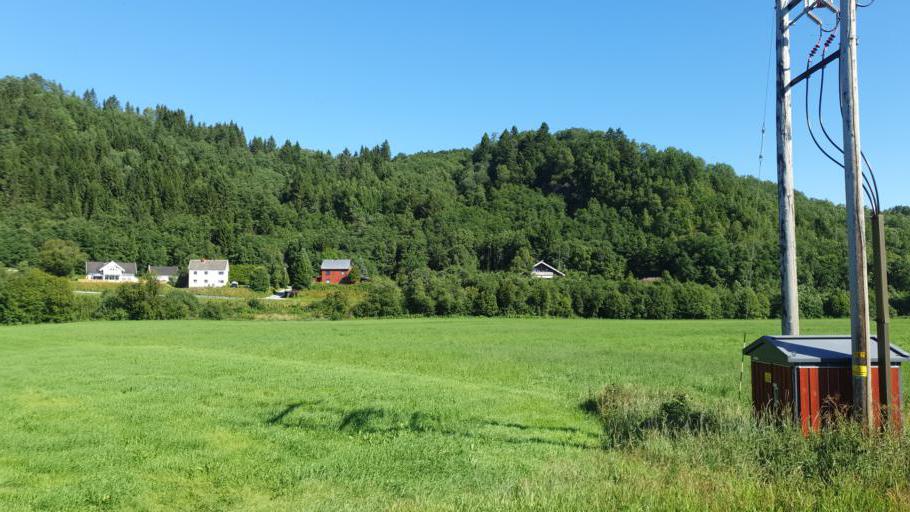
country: NO
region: Sor-Trondelag
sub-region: Orkdal
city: Orkanger
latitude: 63.2097
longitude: 9.7874
